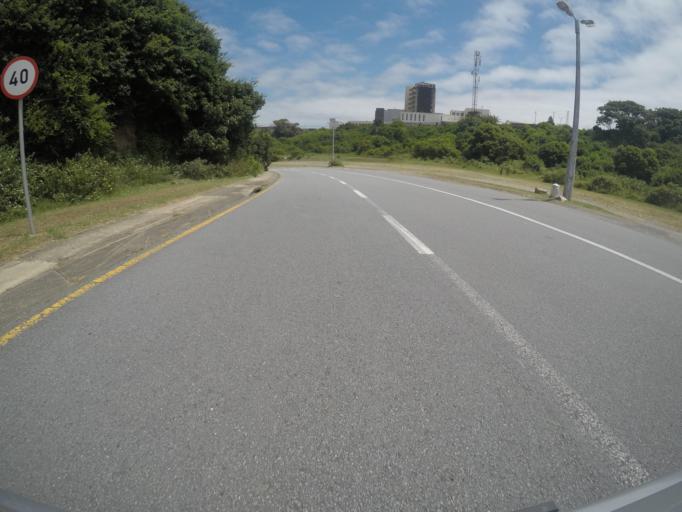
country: ZA
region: Eastern Cape
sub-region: Buffalo City Metropolitan Municipality
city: East London
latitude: -33.0204
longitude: 27.9093
